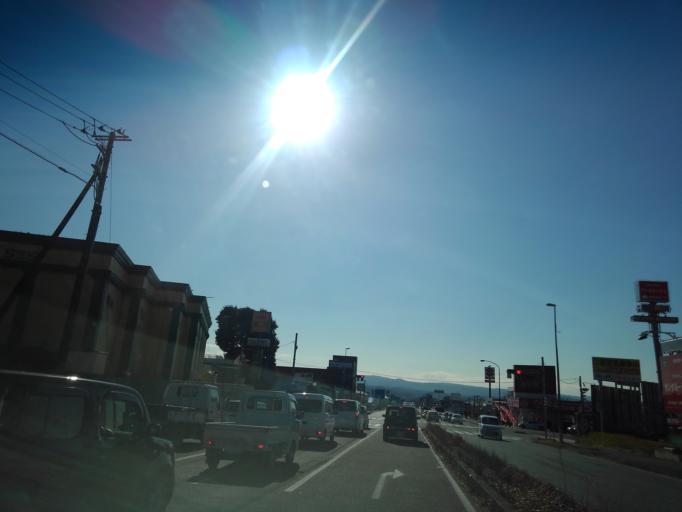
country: JP
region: Chiba
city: Kimitsu
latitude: 35.3340
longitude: 139.9227
